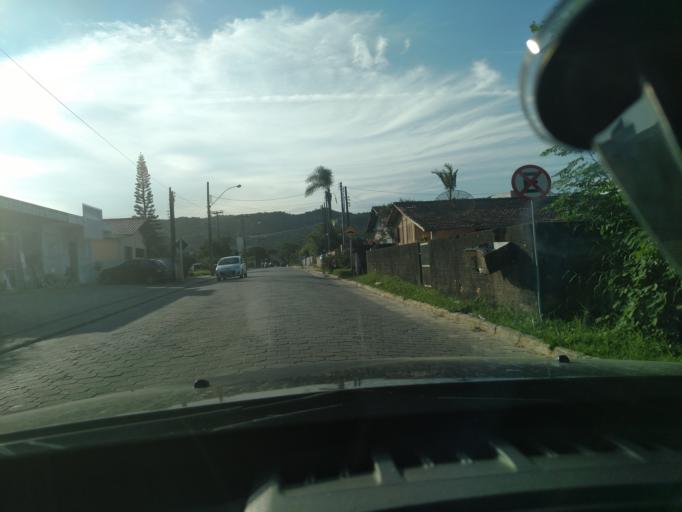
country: BR
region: Santa Catarina
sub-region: Porto Belo
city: Porto Belo
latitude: -27.1503
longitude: -48.5074
